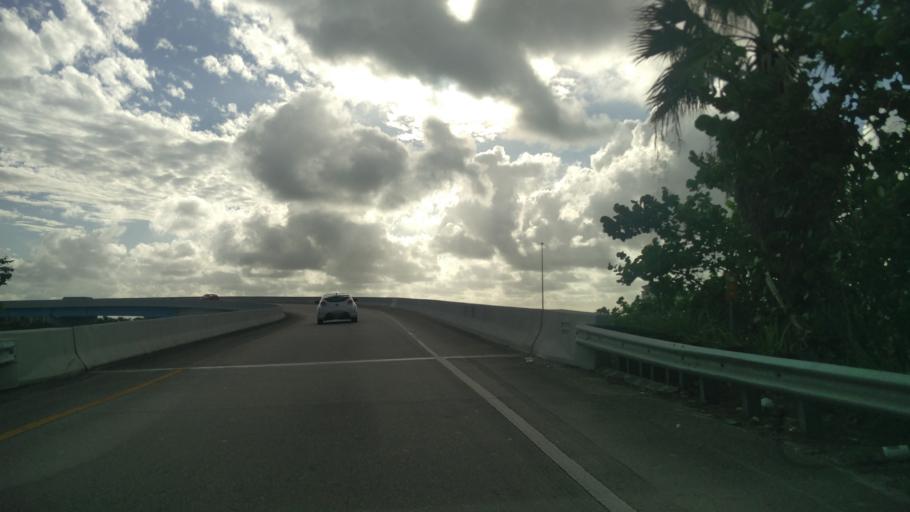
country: US
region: Florida
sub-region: Palm Beach County
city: North Palm Beach
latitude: 26.8419
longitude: -80.1014
